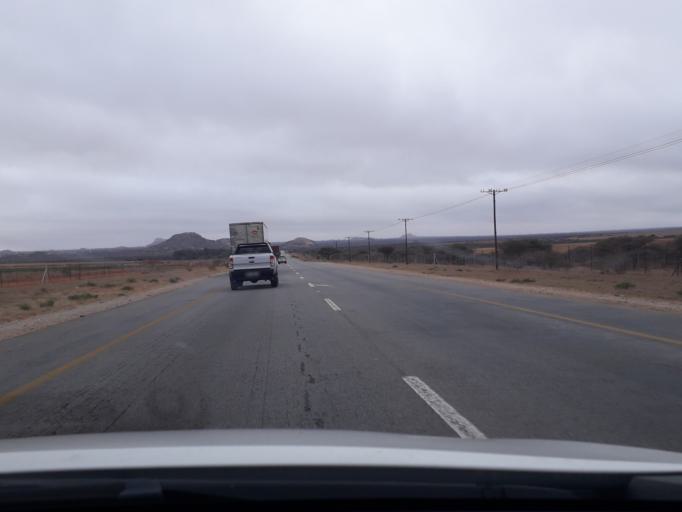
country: ZA
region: Limpopo
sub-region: Capricorn District Municipality
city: Mankoeng
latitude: -23.5566
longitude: 29.6862
